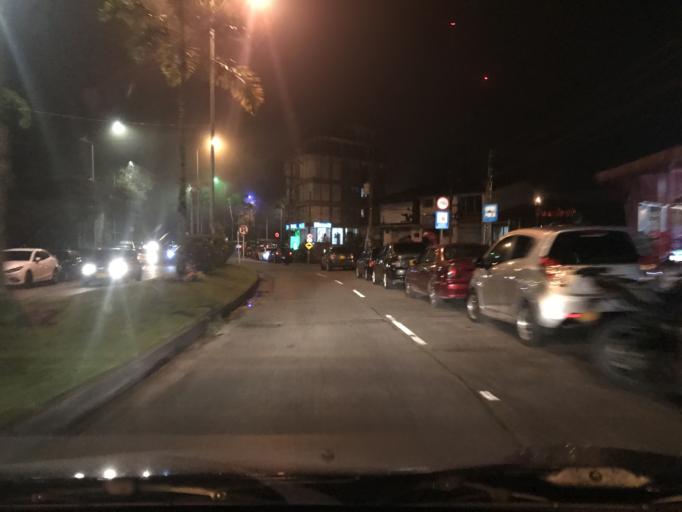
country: CO
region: Caldas
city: Manizales
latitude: 5.0748
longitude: -75.5277
